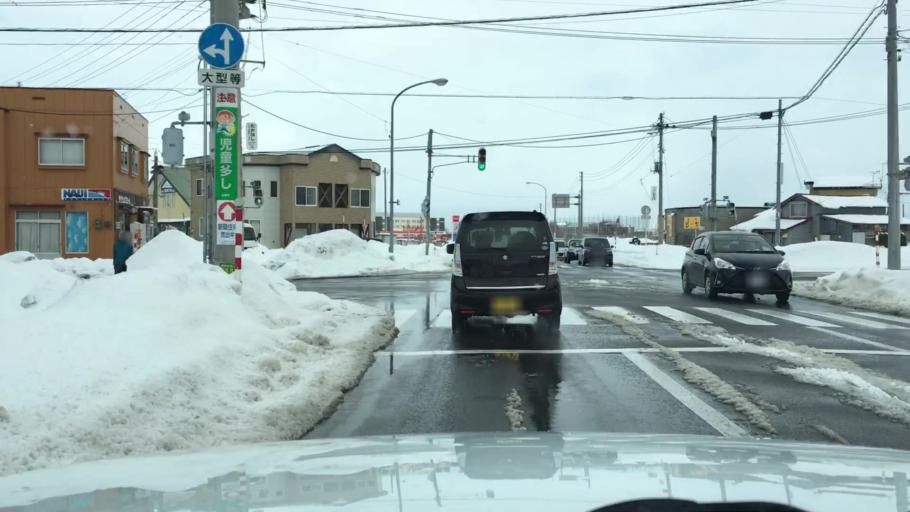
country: JP
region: Aomori
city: Hirosaki
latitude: 40.5818
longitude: 140.4971
